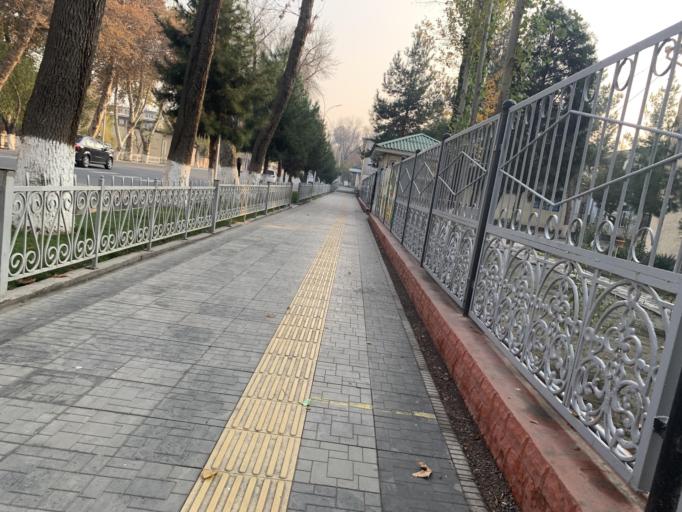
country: UZ
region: Fergana
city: Qo`qon
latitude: 40.5321
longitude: 70.9379
